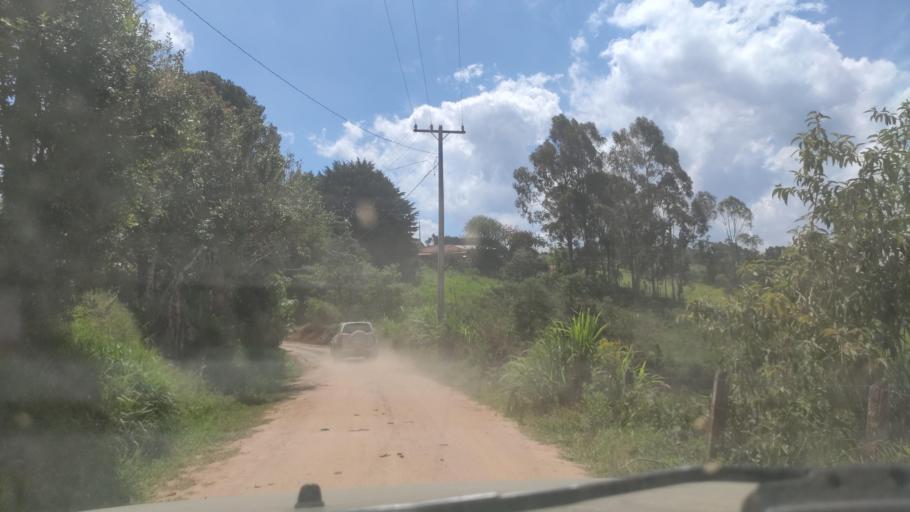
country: BR
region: Minas Gerais
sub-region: Cambui
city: Cambui
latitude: -22.7031
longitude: -46.0138
